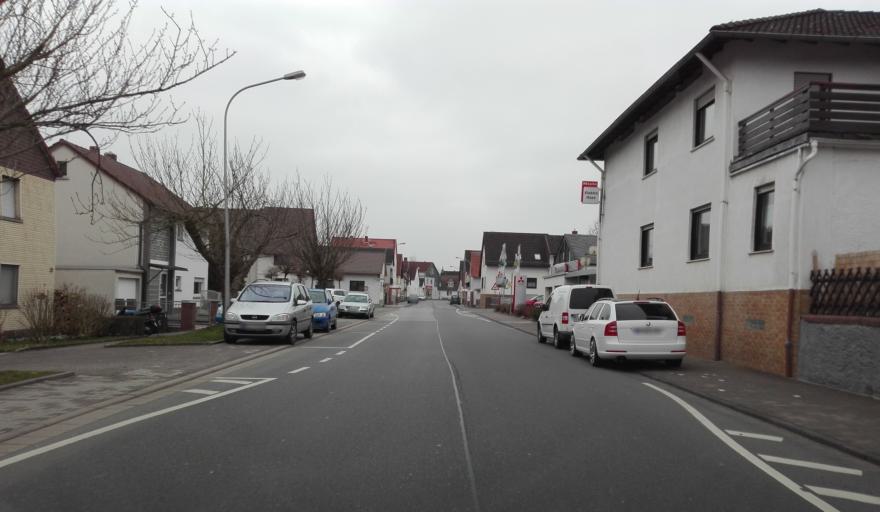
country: DE
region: Hesse
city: Ober-Ramstadt
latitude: 49.8050
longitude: 8.7372
